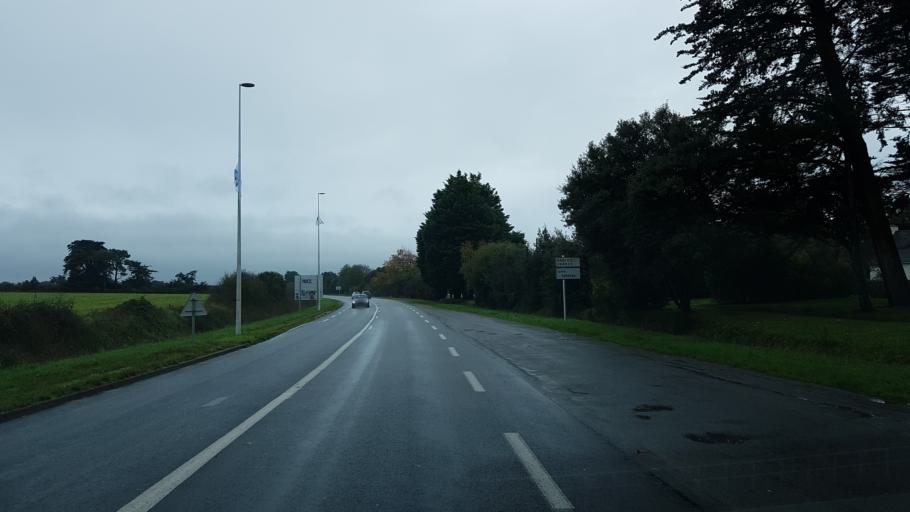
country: FR
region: Brittany
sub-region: Departement du Morbihan
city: Arzon
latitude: 47.5405
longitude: -2.8778
